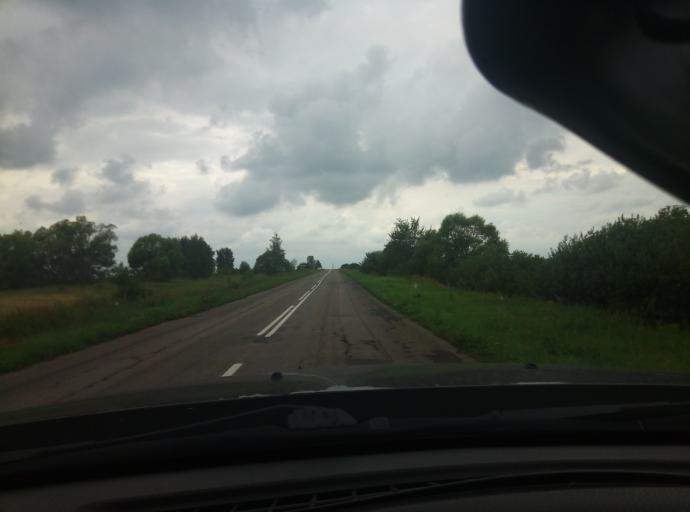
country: RU
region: Tula
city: Begichevskiy
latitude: 53.8460
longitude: 38.2716
